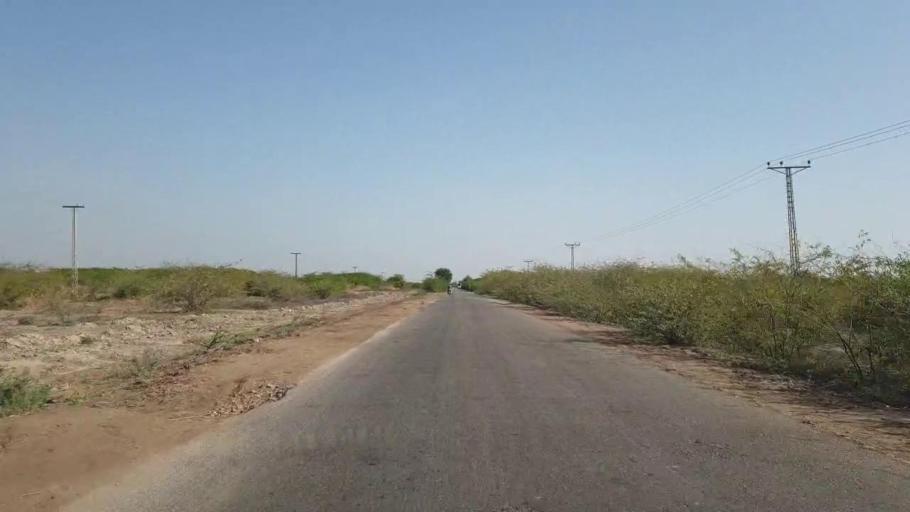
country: PK
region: Sindh
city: Chor
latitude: 25.4700
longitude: 69.7698
